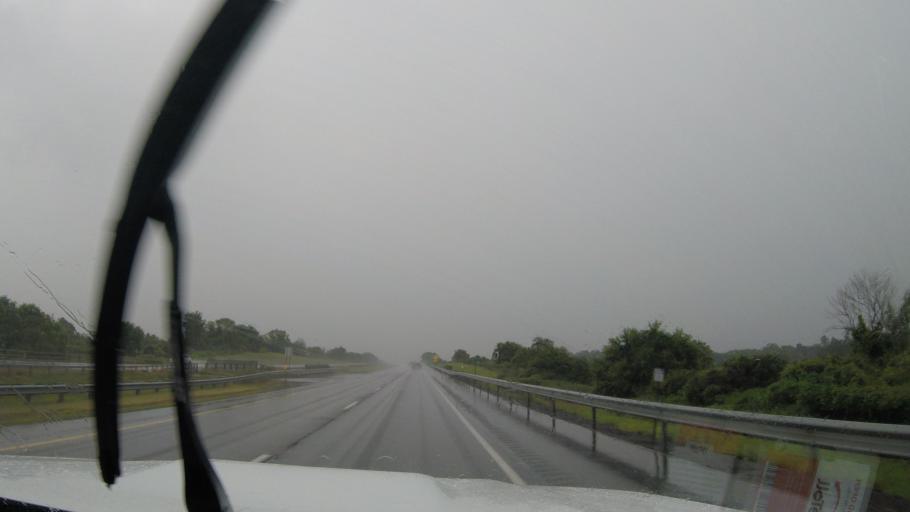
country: US
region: New York
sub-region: Ontario County
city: Phelps
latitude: 42.9553
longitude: -77.0132
